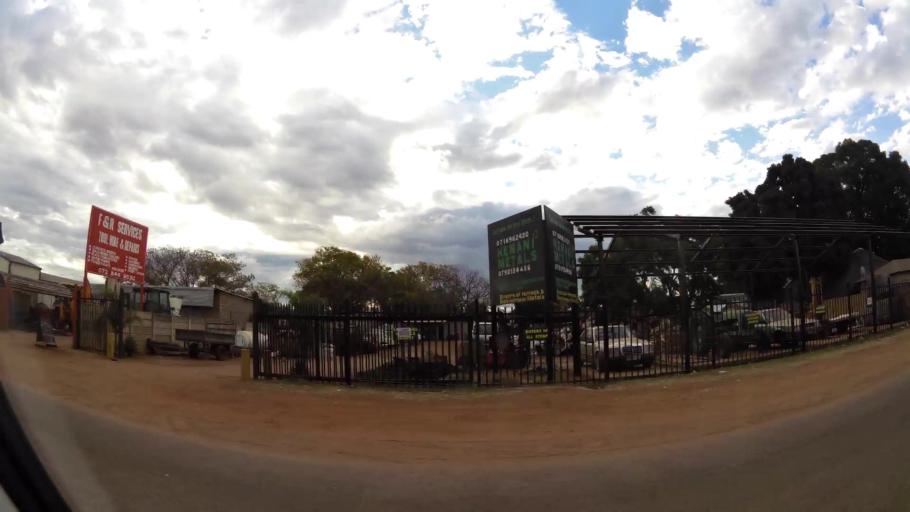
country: ZA
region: Limpopo
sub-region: Waterberg District Municipality
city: Modimolle
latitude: -24.5246
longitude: 28.7125
